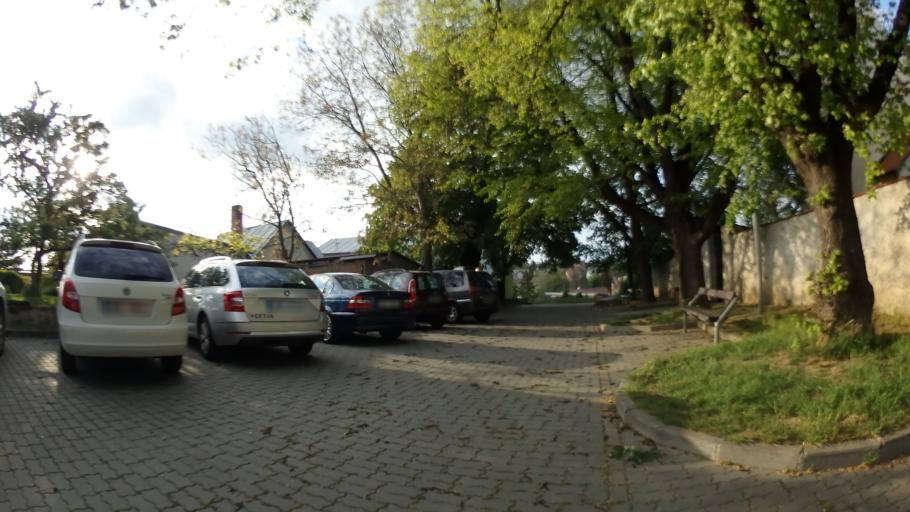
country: CZ
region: South Moravian
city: Moravany
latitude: 49.1441
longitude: 16.5778
